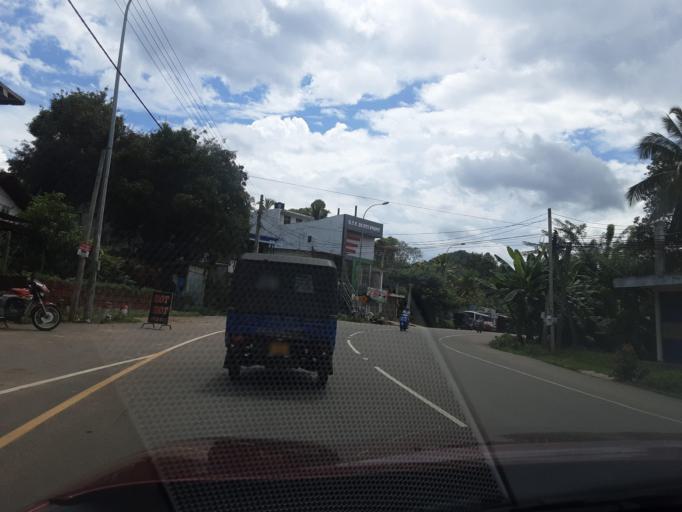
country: LK
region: Uva
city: Monaragala
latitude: 6.8964
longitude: 81.2387
